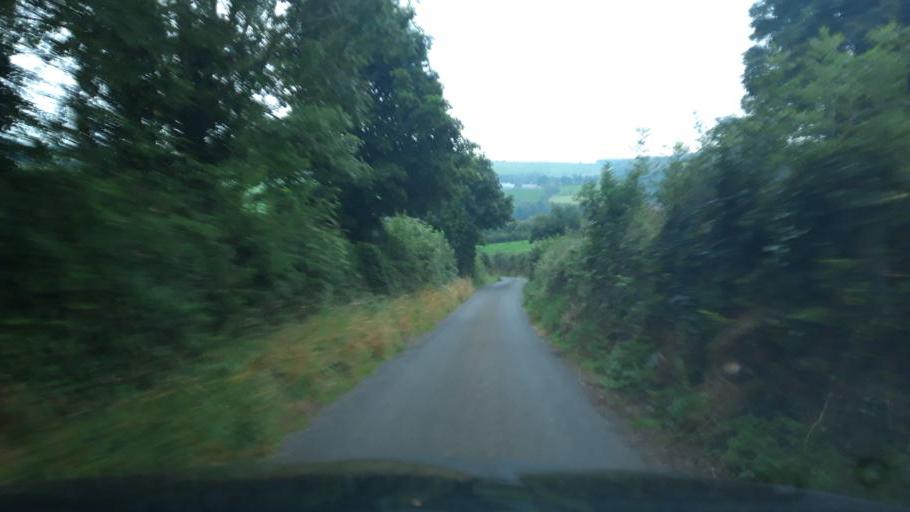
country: IE
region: Leinster
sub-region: Kilkenny
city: Graiguenamanagh
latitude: 52.5777
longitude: -7.0289
